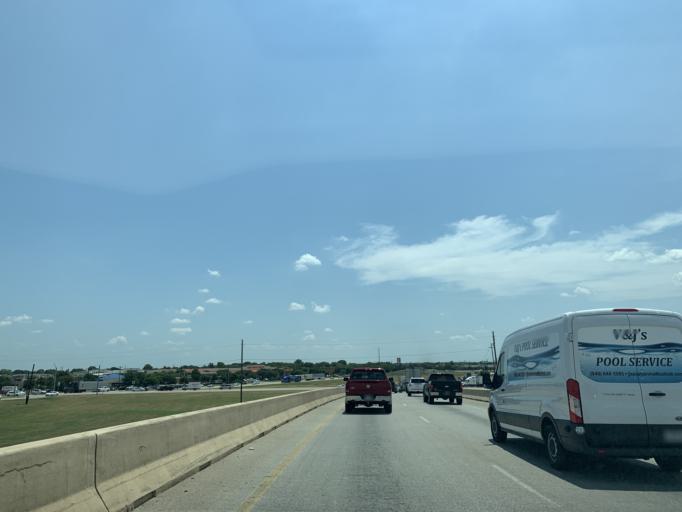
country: US
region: Texas
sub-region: Denton County
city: Roanoke
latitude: 33.0128
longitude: -97.2234
